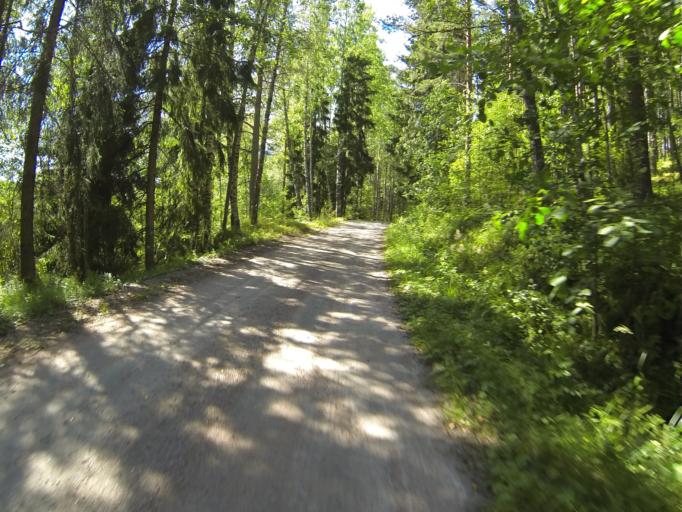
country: FI
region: Varsinais-Suomi
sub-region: Salo
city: Pernioe
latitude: 60.2889
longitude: 23.0806
